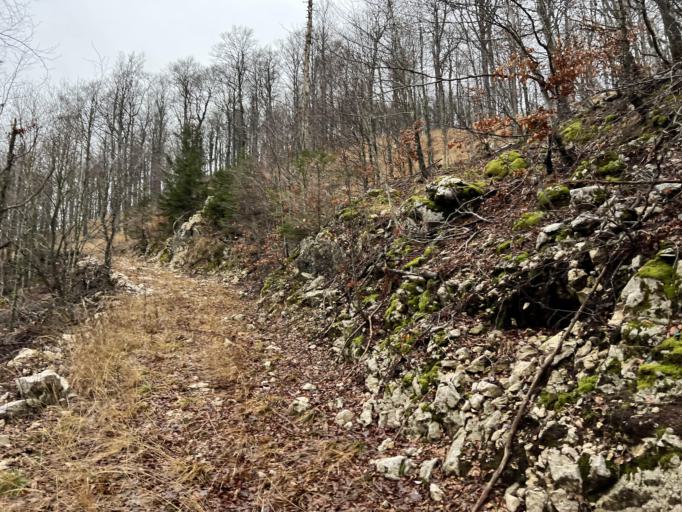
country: SI
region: Nova Gorica
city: Sempas
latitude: 45.9507
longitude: 13.8189
